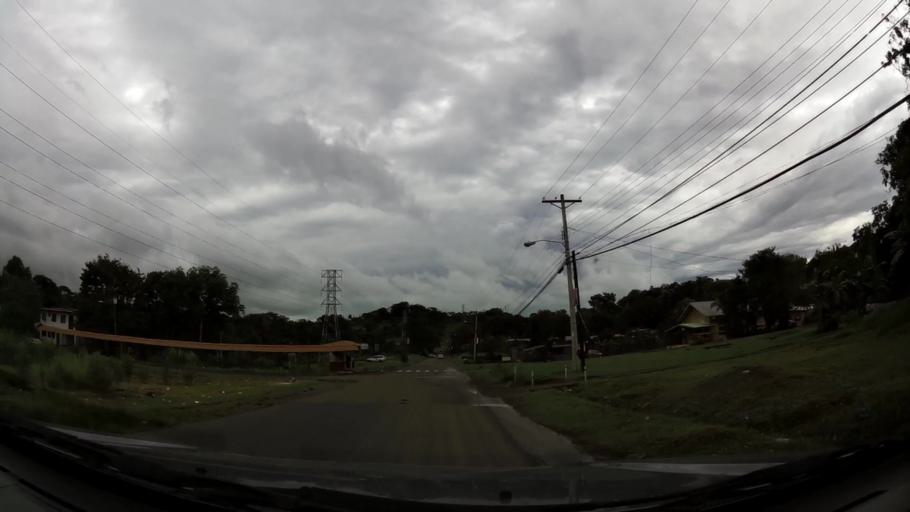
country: PA
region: Panama
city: Chilibre
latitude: 9.1629
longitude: -79.6170
